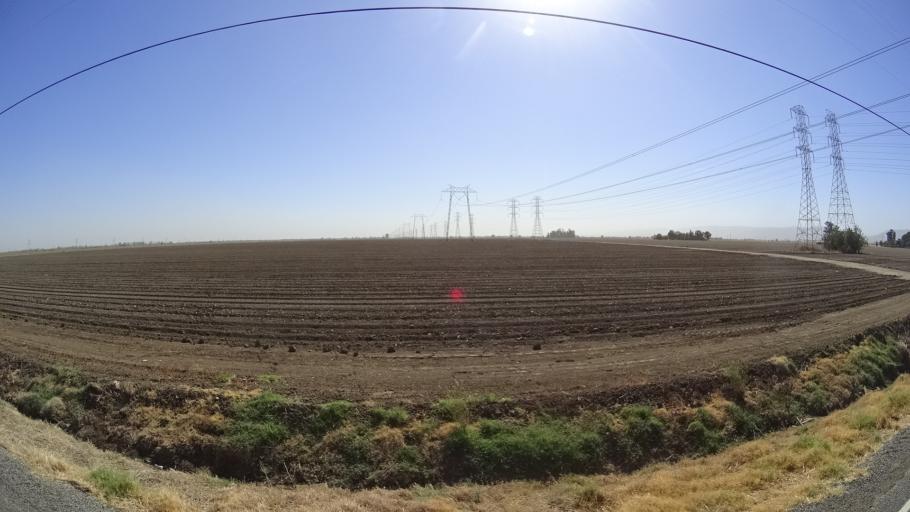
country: US
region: California
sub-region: Yolo County
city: Winters
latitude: 38.5843
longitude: -121.9286
